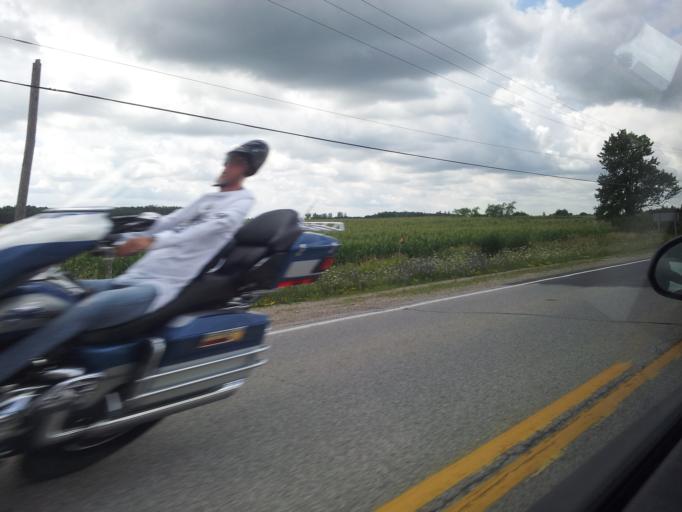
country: CA
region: Ontario
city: Stratford
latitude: 43.3697
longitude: -80.8481
